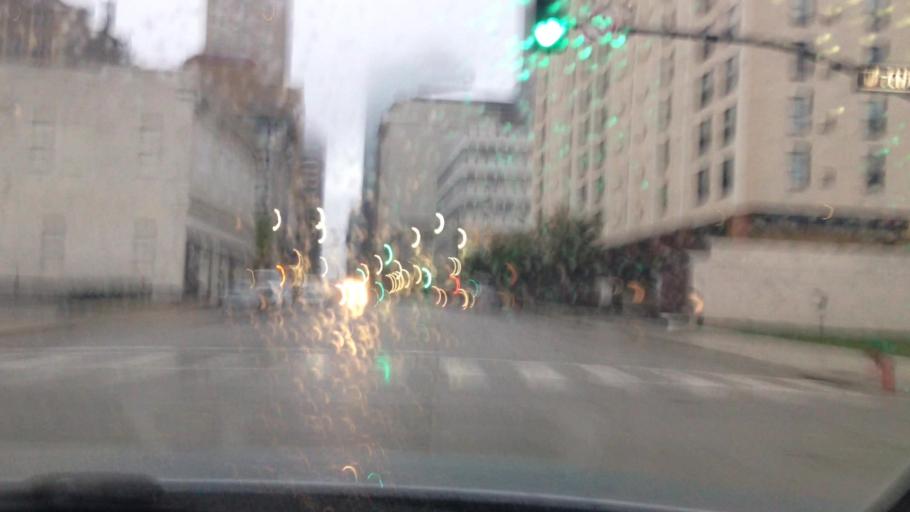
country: US
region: Missouri
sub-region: Jackson County
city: Kansas City
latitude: 39.1056
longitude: -94.5817
